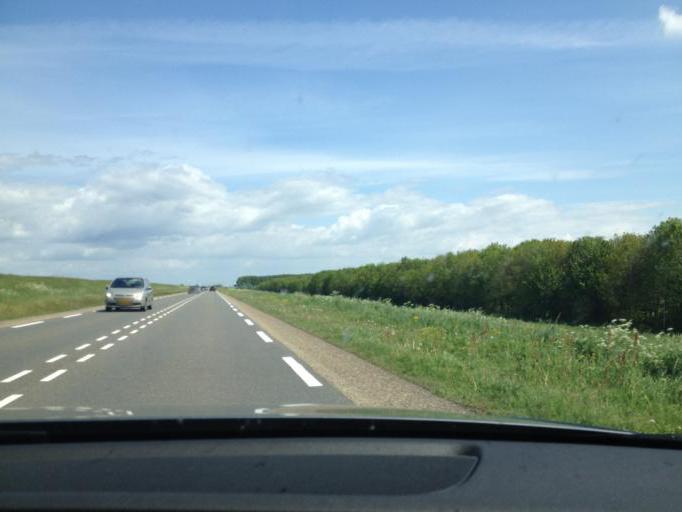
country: NL
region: Flevoland
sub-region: Gemeente Lelystad
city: Lelystad
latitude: 52.5375
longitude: 5.4498
